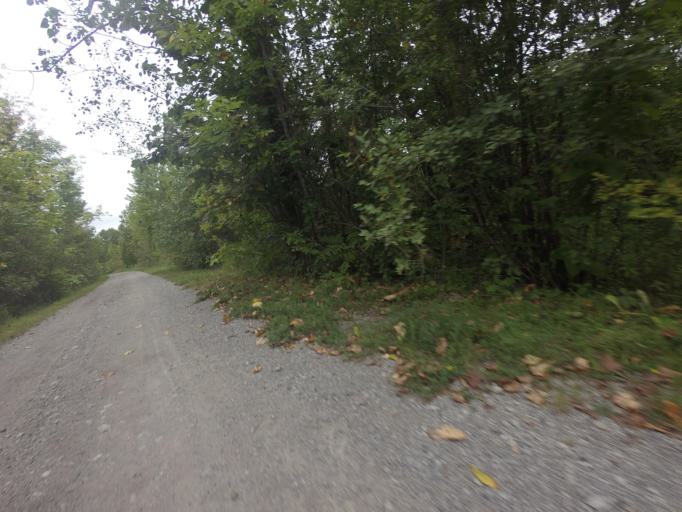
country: CA
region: Ontario
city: Omemee
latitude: 44.3983
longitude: -78.7570
